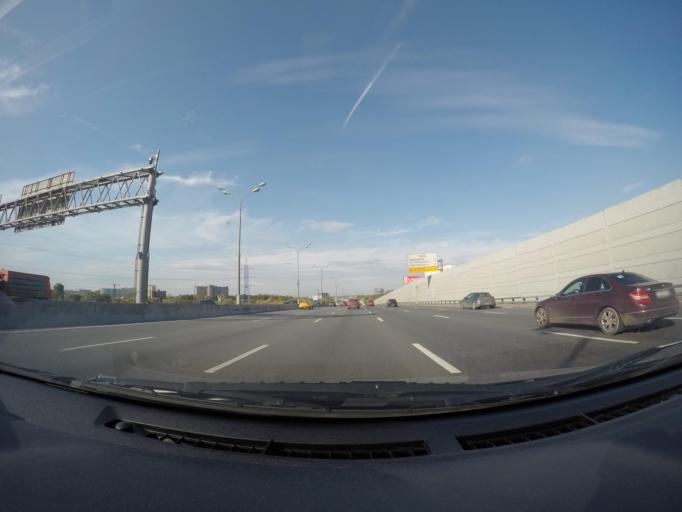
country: RU
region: Moscow
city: Yaroslavskiy
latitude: 55.8861
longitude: 37.7188
